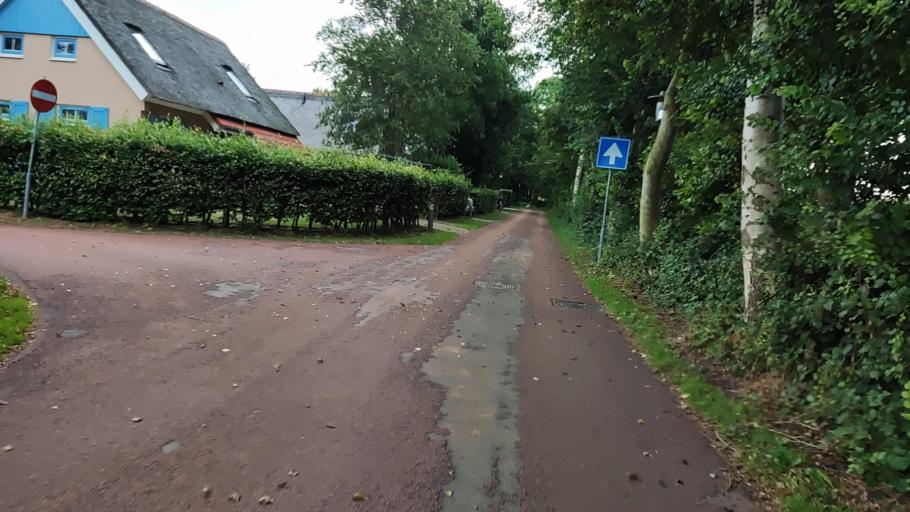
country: NL
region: North Holland
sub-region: Gemeente Texel
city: Den Burg
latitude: 53.0870
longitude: 4.7684
